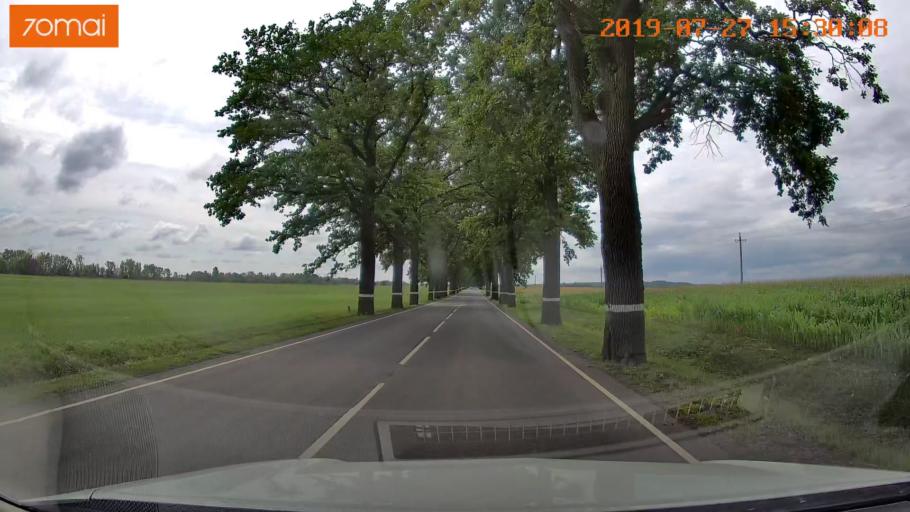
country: RU
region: Kaliningrad
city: Nesterov
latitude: 54.6290
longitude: 22.5175
